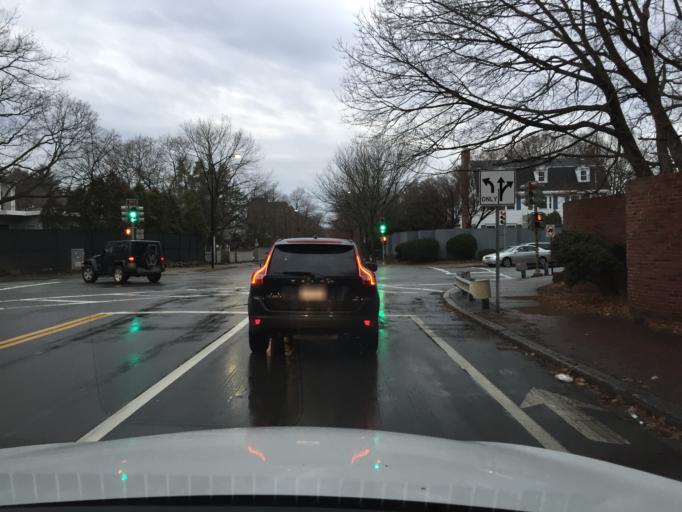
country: US
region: Massachusetts
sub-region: Middlesex County
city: Cambridge
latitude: 42.3763
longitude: -71.1404
